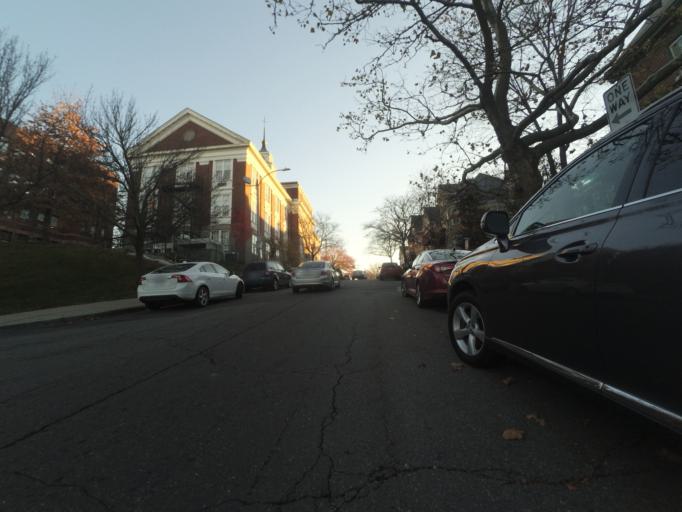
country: US
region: Massachusetts
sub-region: Middlesex County
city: Somerville
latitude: 42.3878
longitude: -71.0981
